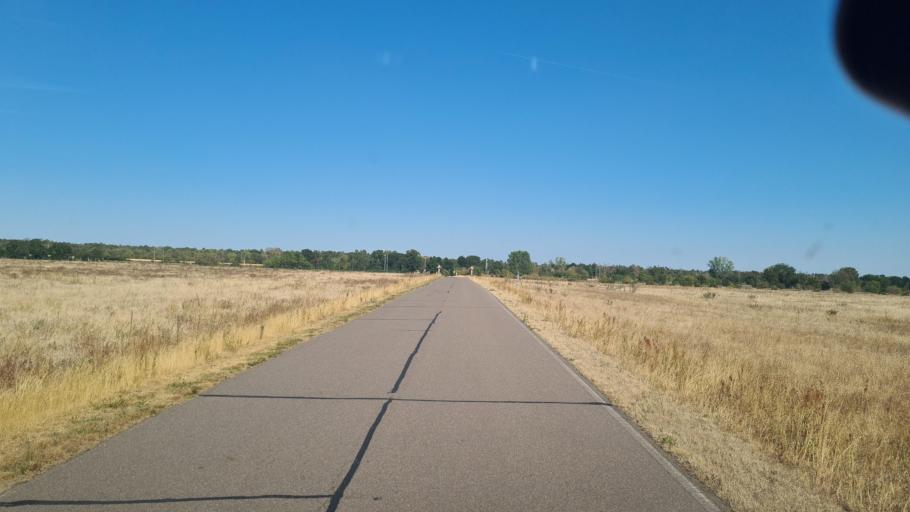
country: DE
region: Saxony
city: Zeithain
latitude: 51.3815
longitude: 13.3066
